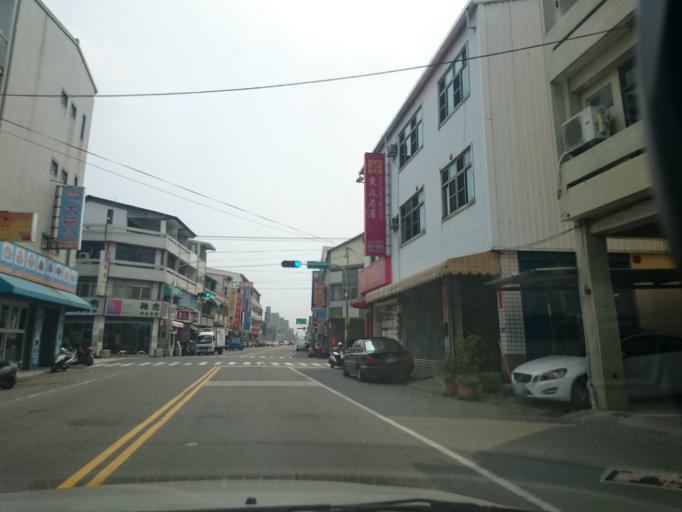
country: TW
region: Taiwan
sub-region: Nantou
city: Nantou
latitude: 23.8747
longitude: 120.5283
